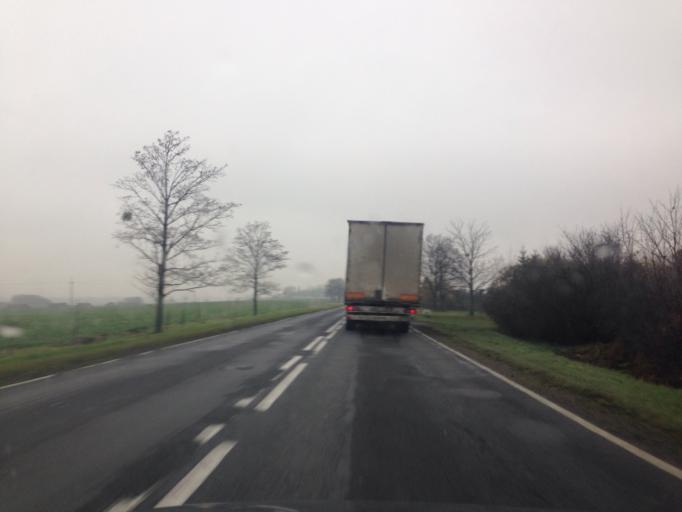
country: PL
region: Kujawsko-Pomorskie
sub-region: Powiat nakielski
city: Slesin
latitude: 53.1638
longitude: 17.6552
